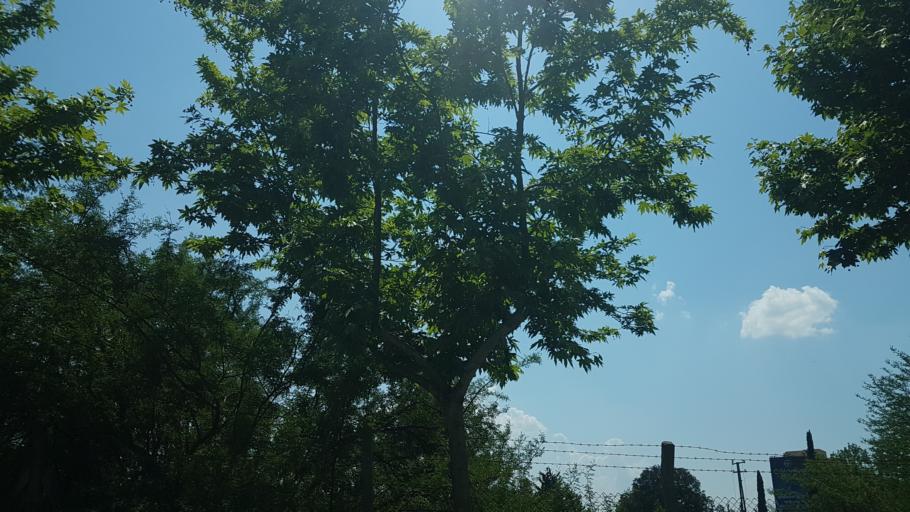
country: TR
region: Adana
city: Adana
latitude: 37.0263
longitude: 35.3610
